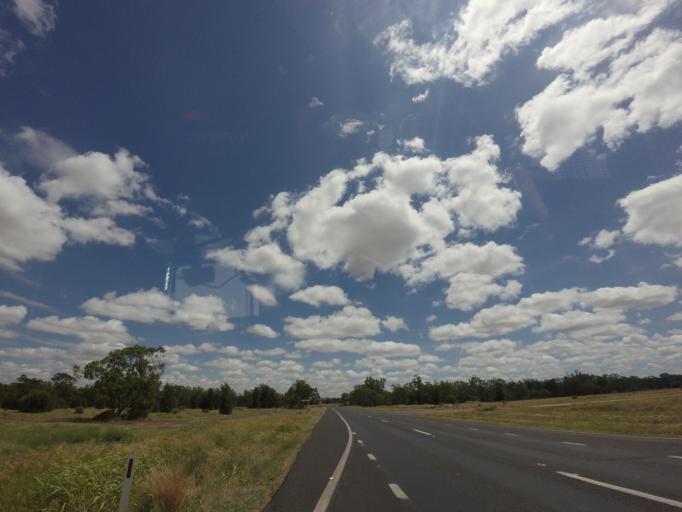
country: AU
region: New South Wales
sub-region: Moree Plains
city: Moree
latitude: -29.1815
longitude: 150.0096
